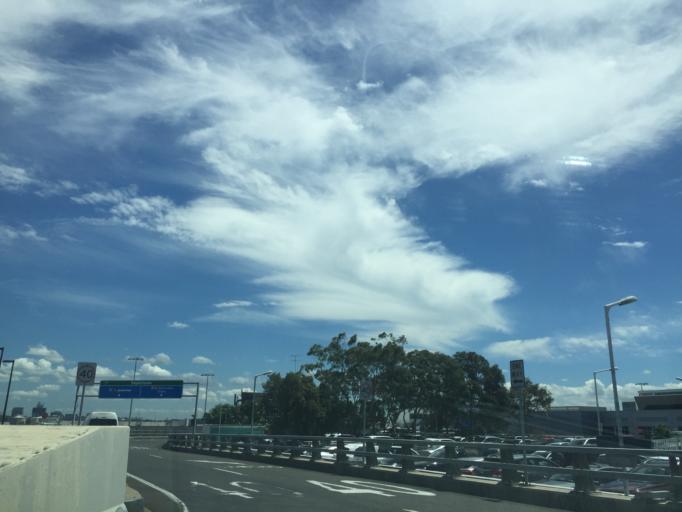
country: AU
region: New South Wales
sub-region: Botany Bay
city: Mascot
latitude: -33.9336
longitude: 151.1792
